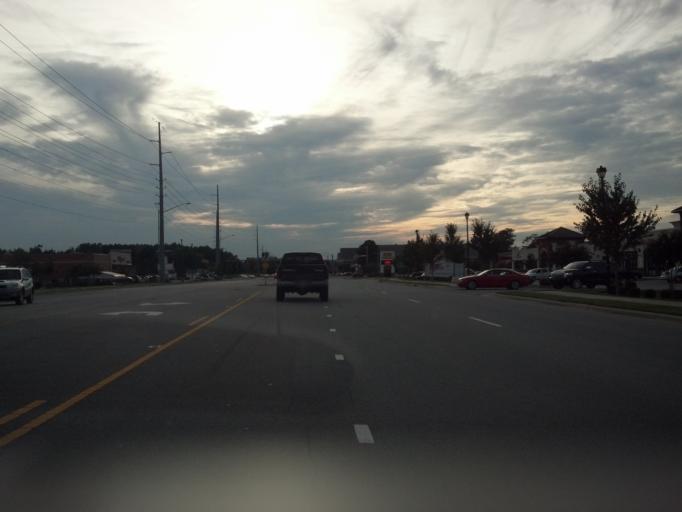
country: US
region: North Carolina
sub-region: Pitt County
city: Winterville
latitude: 35.5481
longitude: -77.4022
